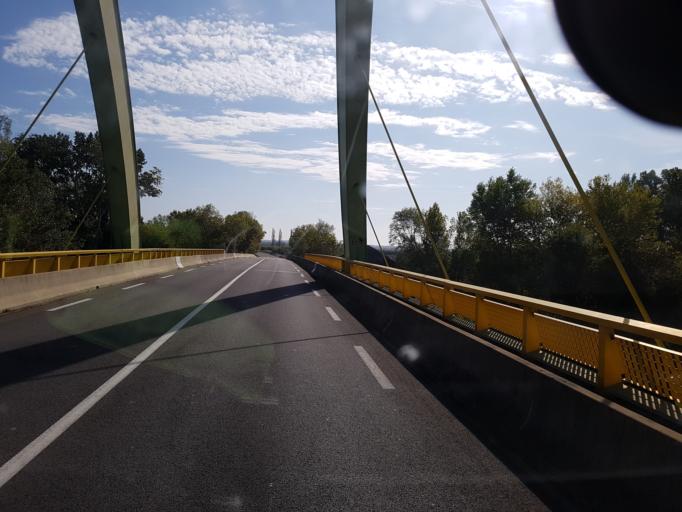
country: FR
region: Languedoc-Roussillon
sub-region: Departement du Gard
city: Saint-Gilles
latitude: 43.6655
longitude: 4.4531
